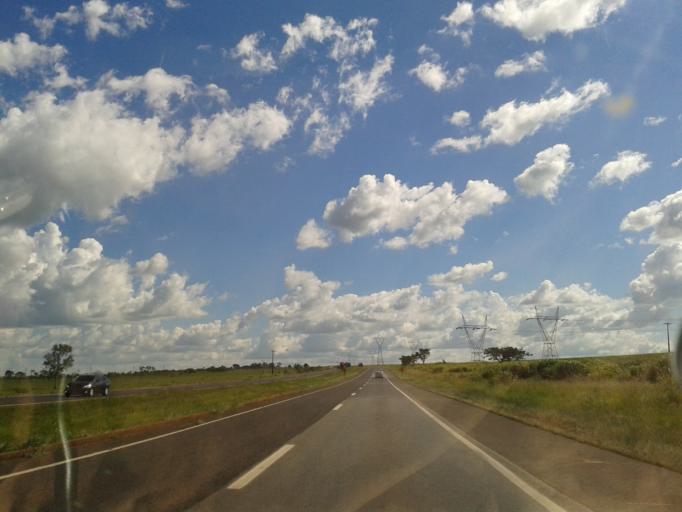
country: BR
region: Goias
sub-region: Goiatuba
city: Goiatuba
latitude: -17.8839
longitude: -49.2316
